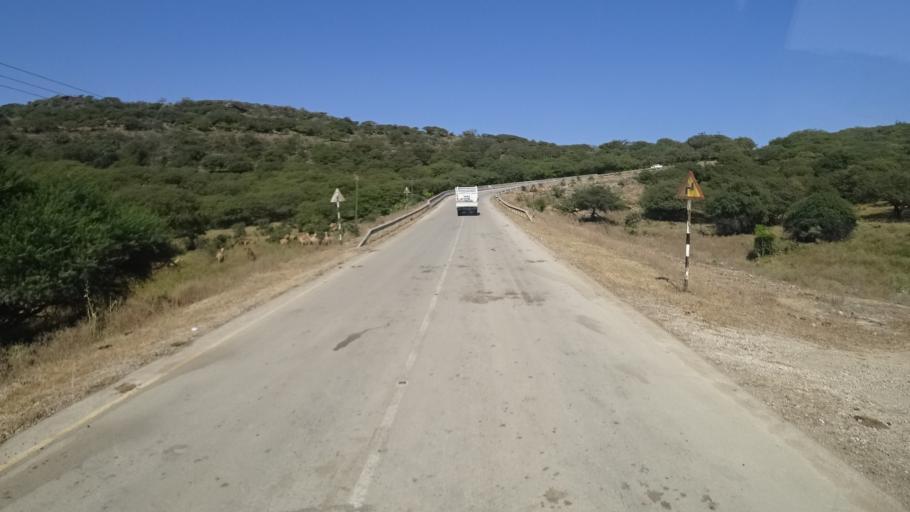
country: OM
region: Zufar
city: Salalah
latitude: 17.0699
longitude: 54.6007
